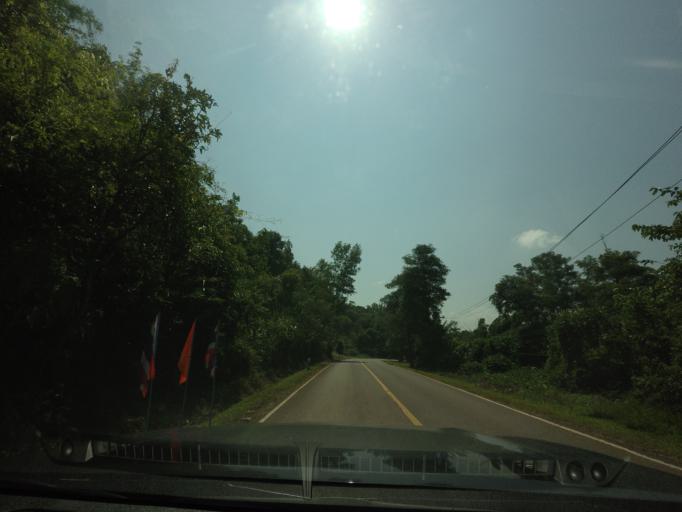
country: TH
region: Nan
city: Bo Kluea
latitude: 19.0720
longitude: 101.1588
